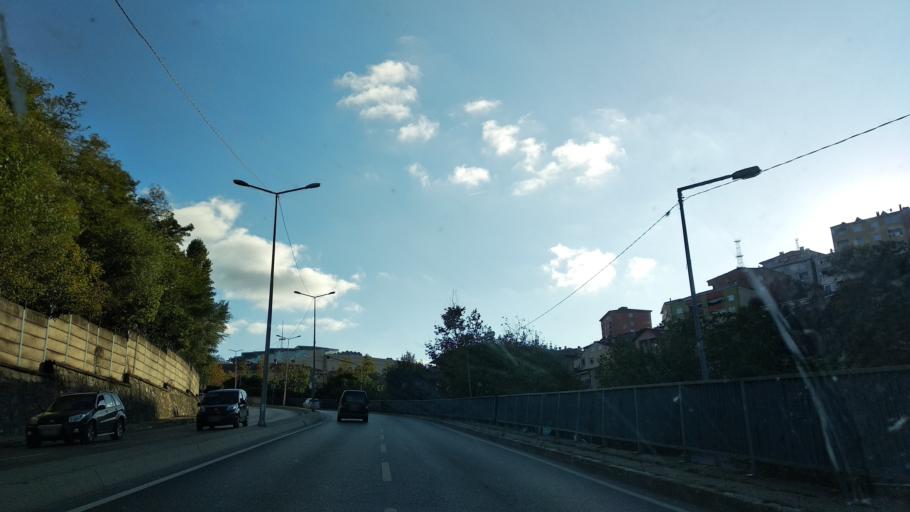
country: TR
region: Istanbul
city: Sisli
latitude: 41.1147
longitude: 29.0348
